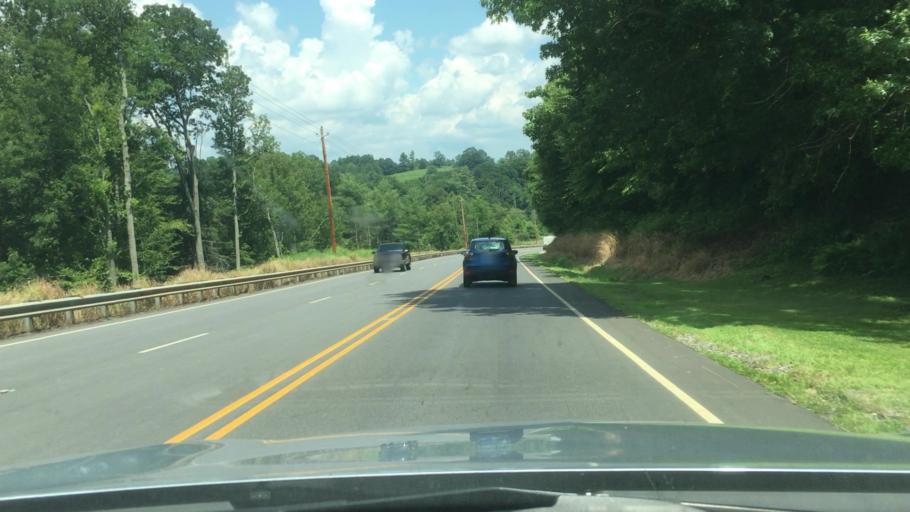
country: US
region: North Carolina
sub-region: Madison County
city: Mars Hill
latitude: 35.8255
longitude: -82.6192
